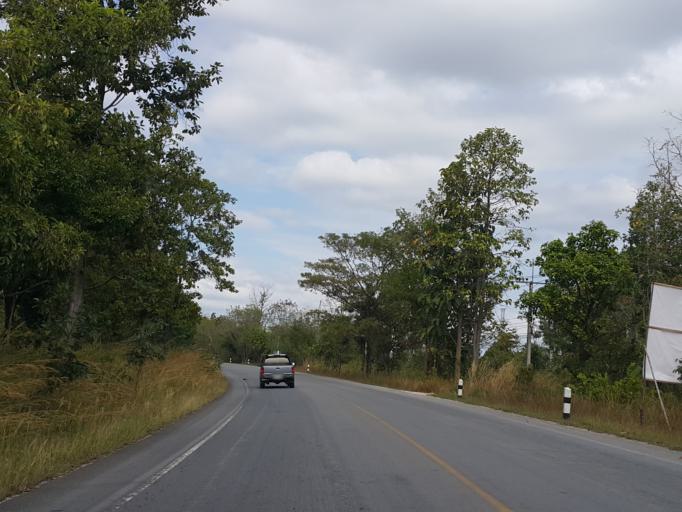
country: TH
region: Lampang
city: Lampang
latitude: 18.3881
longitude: 99.4599
